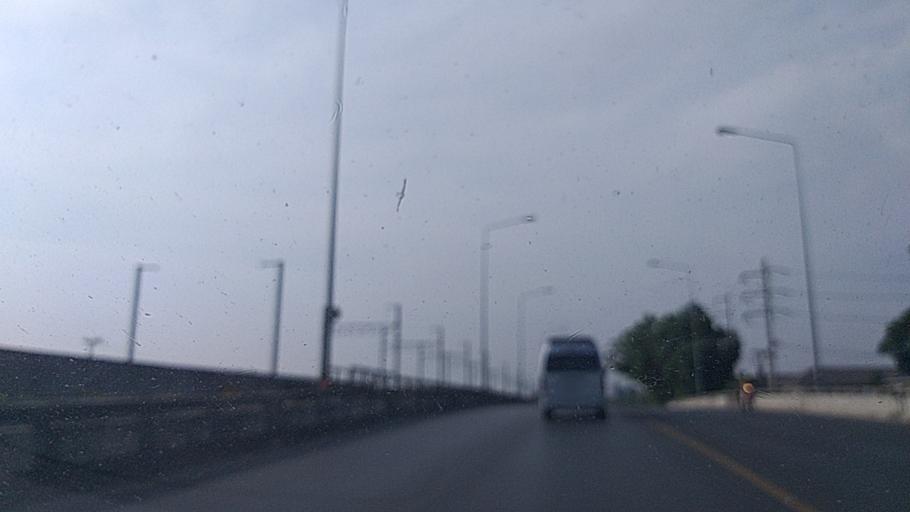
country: TH
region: Phra Nakhon Si Ayutthaya
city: Ban Bang Kadi Pathum Thani
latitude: 13.9811
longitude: 100.6032
